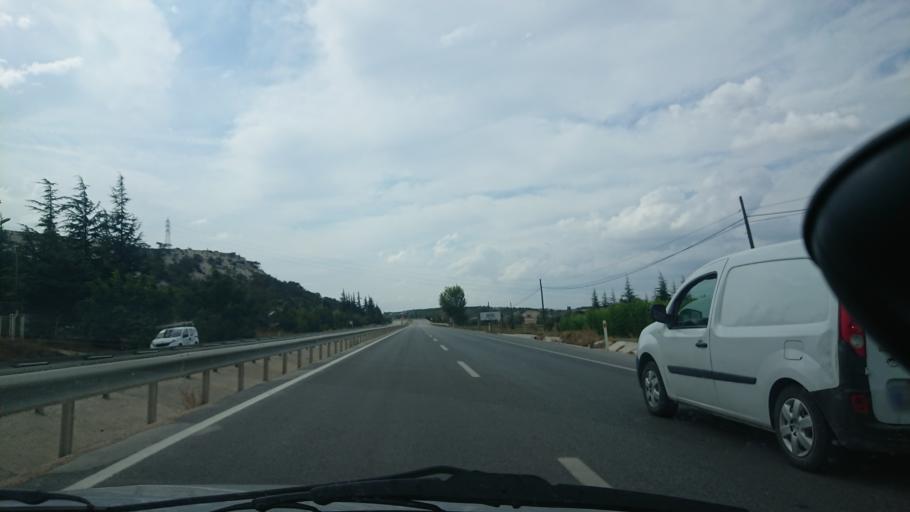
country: TR
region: Eskisehir
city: Eskisehir
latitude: 39.7272
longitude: 30.3585
